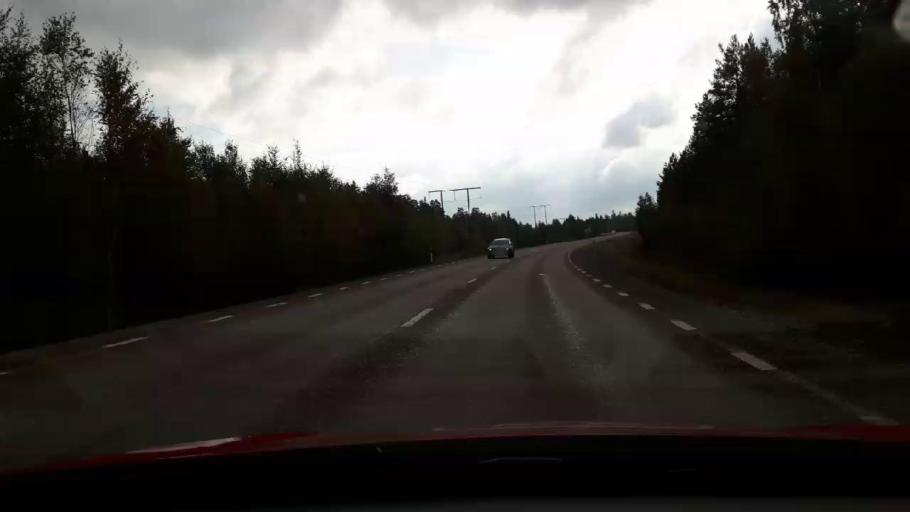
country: SE
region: Gaevleborg
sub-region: Soderhamns Kommun
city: Ljusne
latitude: 61.0951
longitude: 16.9546
